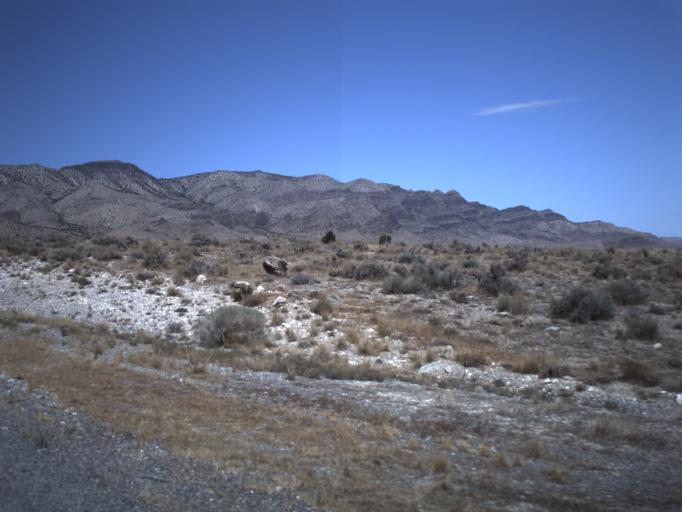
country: US
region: Utah
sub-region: Beaver County
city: Milford
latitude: 39.0859
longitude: -113.5265
